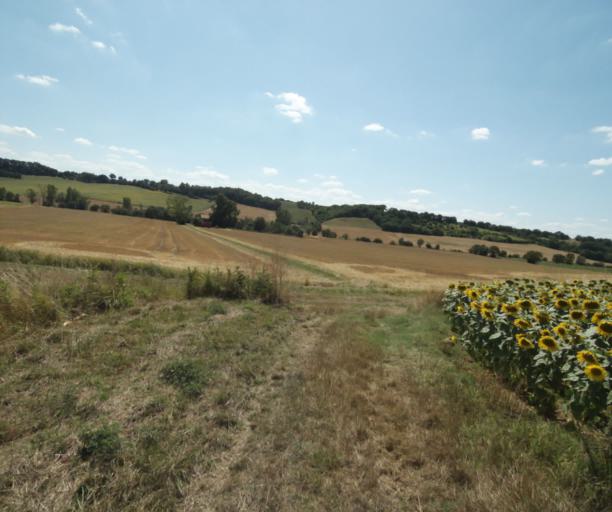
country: FR
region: Midi-Pyrenees
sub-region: Departement de la Haute-Garonne
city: Auriac-sur-Vendinelle
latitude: 43.4998
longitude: 1.8682
